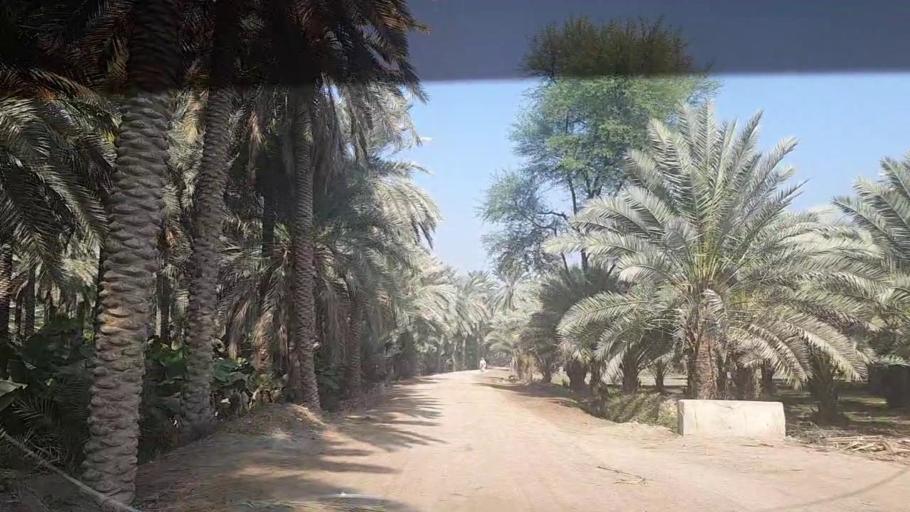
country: PK
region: Sindh
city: Khairpur
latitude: 27.4646
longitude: 68.7173
